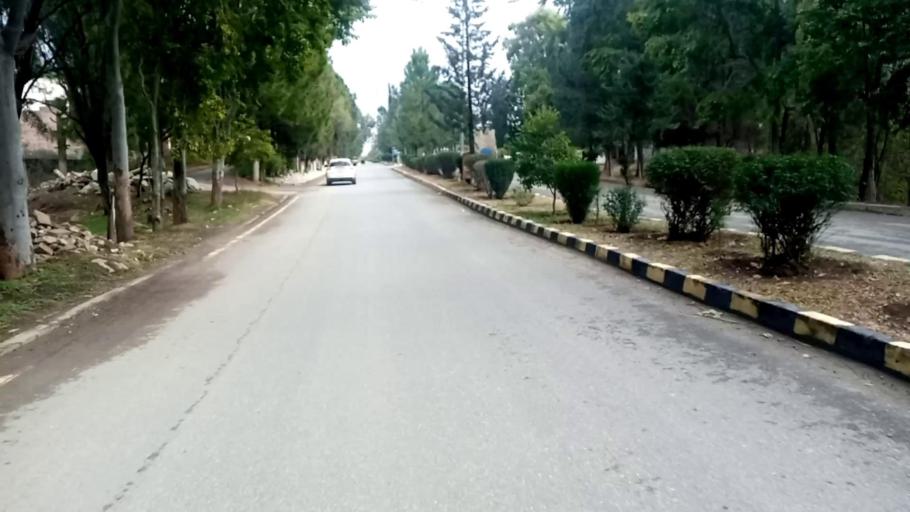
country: PK
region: Khyber Pakhtunkhwa
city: Mingora
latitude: 34.8305
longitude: 72.3475
